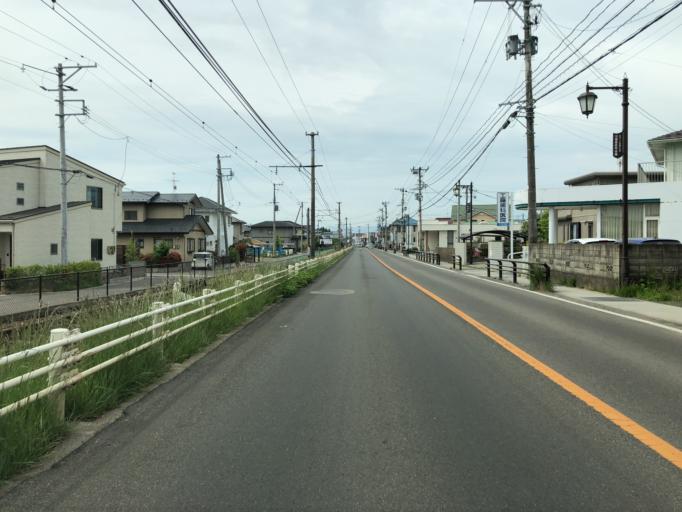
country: JP
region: Fukushima
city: Fukushima-shi
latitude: 37.8089
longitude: 140.4440
